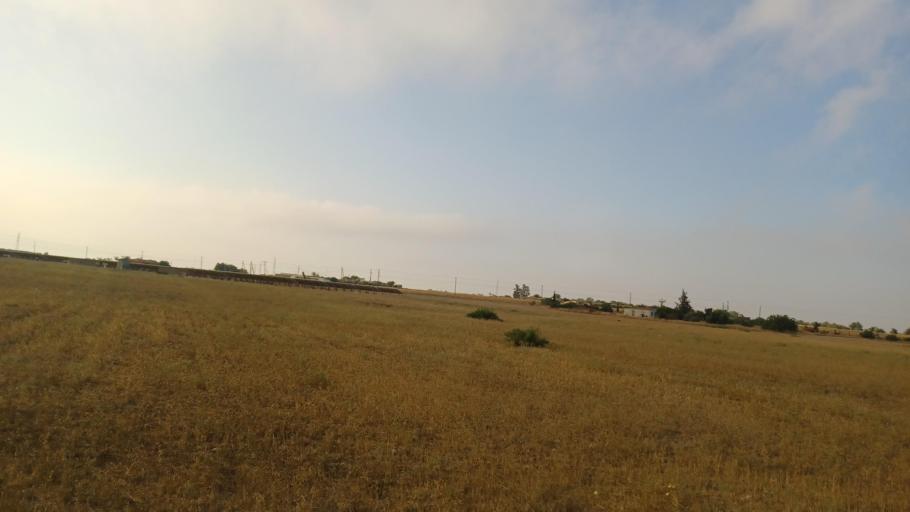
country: CY
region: Ammochostos
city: Avgorou
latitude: 35.0431
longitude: 33.8522
